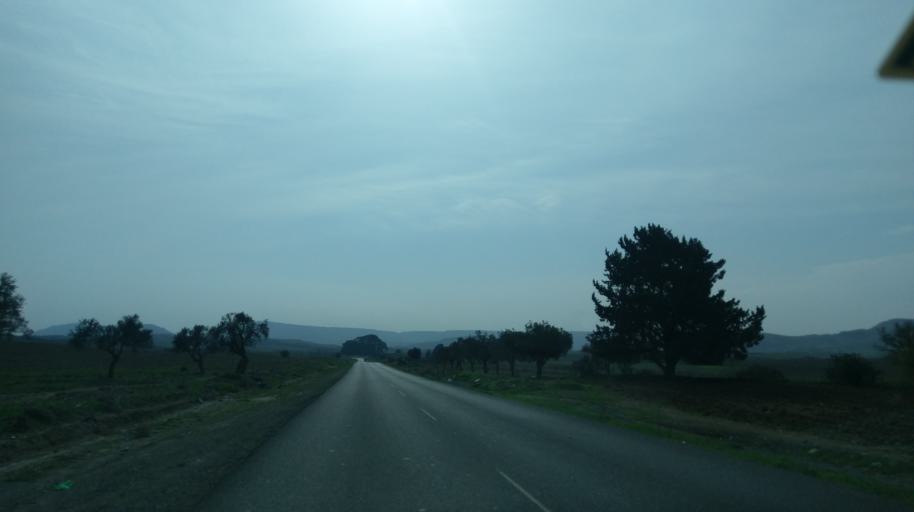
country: CY
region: Keryneia
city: Lapithos
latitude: 35.2907
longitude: 33.0899
